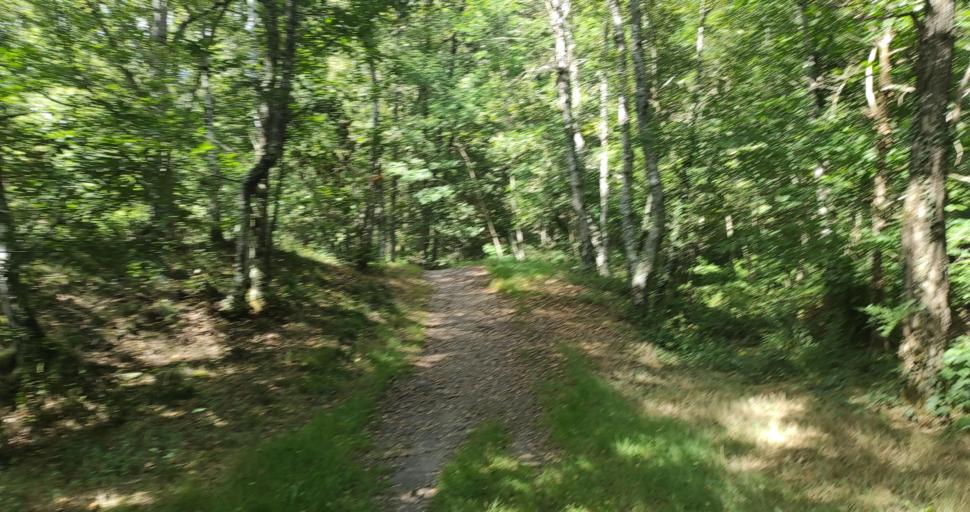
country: FR
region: Midi-Pyrenees
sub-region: Departement de l'Aveyron
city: Cransac
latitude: 44.5356
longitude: 2.2766
